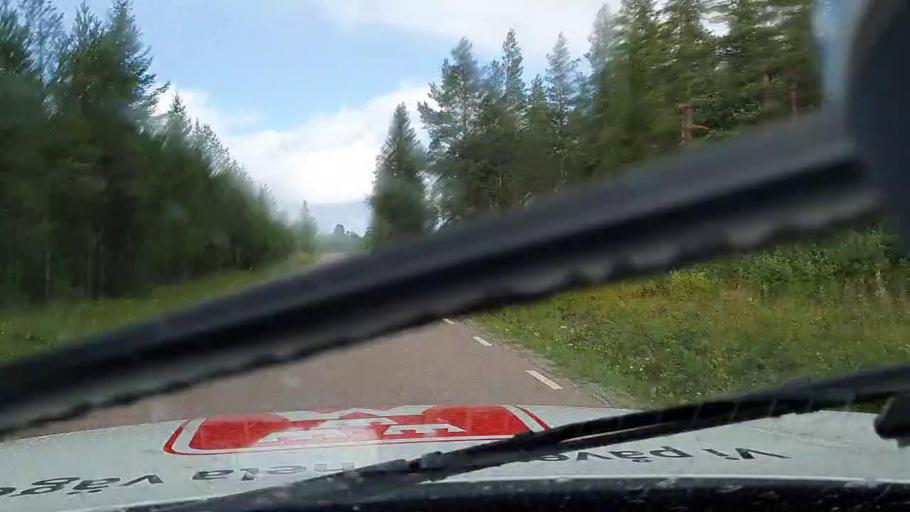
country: SE
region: Jaemtland
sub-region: Stroemsunds Kommun
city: Stroemsund
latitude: 63.8754
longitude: 15.3609
